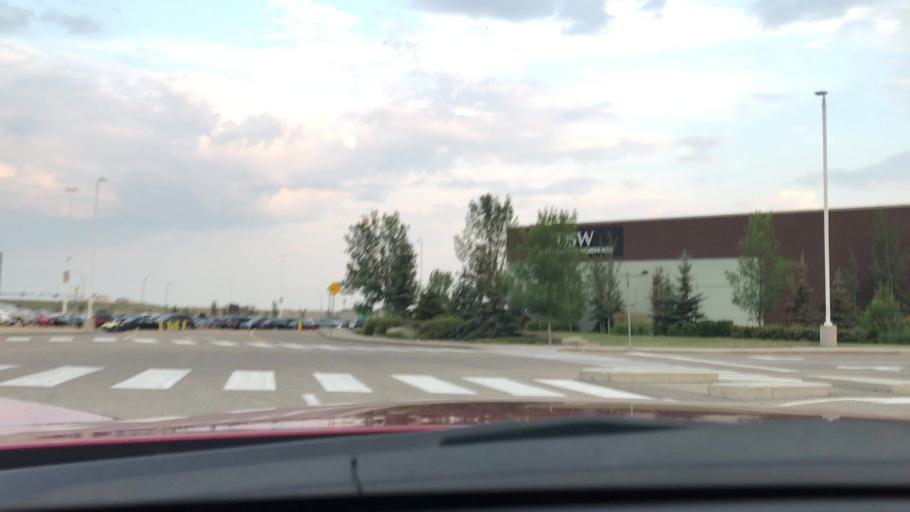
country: CA
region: Alberta
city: Airdrie
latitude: 51.2063
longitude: -113.9927
